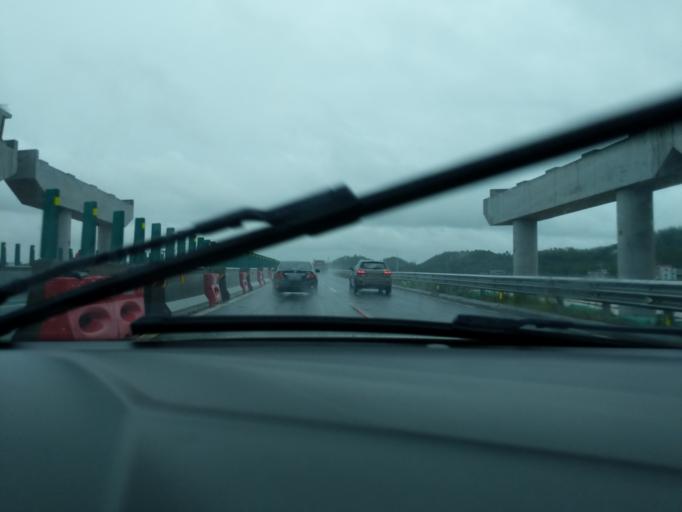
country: CN
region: Guangdong
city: Yueshan
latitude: 22.4631
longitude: 112.7161
